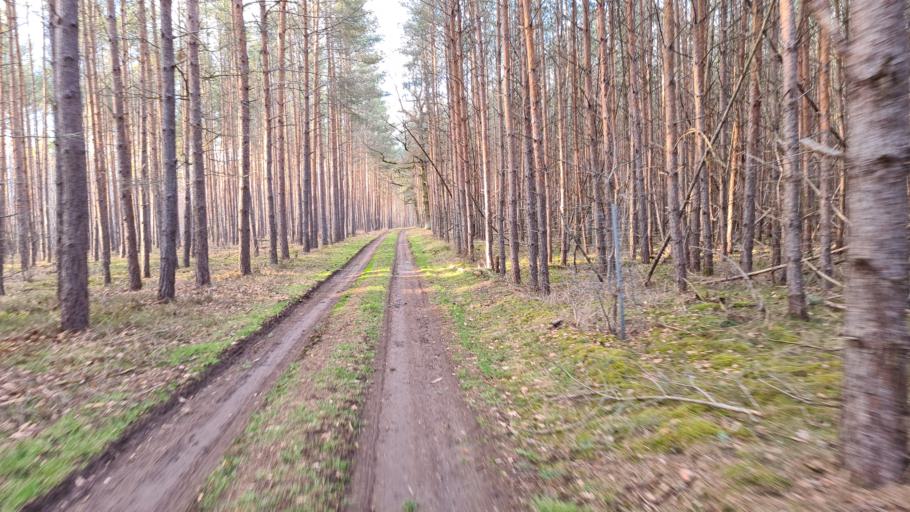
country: DE
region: Brandenburg
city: Falkenberg
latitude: 51.5782
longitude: 13.3133
